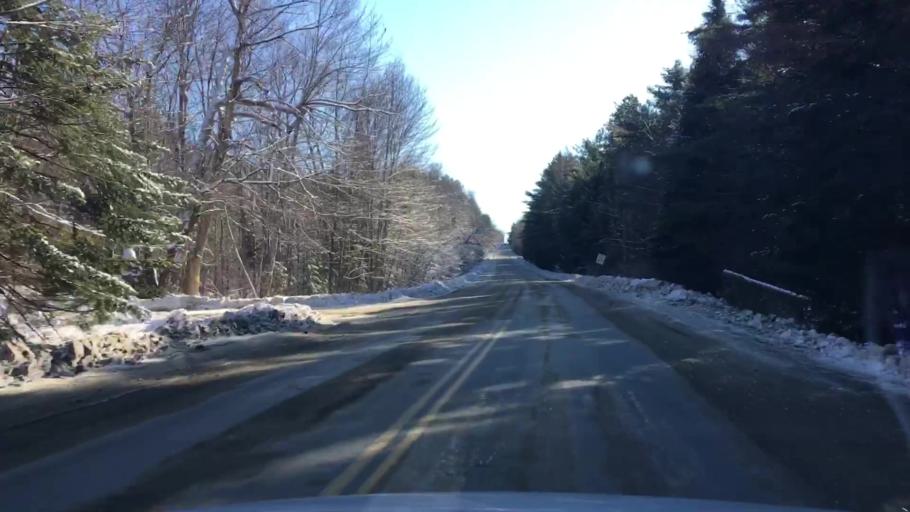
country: US
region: Maine
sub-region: Kennebec County
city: Readfield
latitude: 44.3546
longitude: -69.9914
